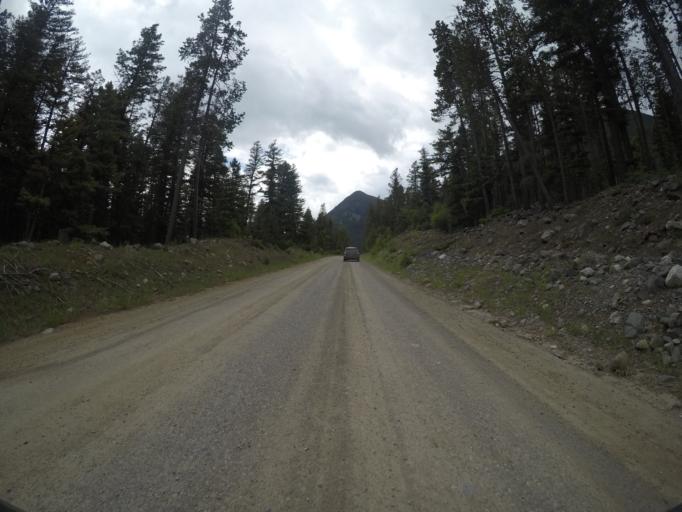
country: US
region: Montana
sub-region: Park County
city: Livingston
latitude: 45.4987
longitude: -110.2265
